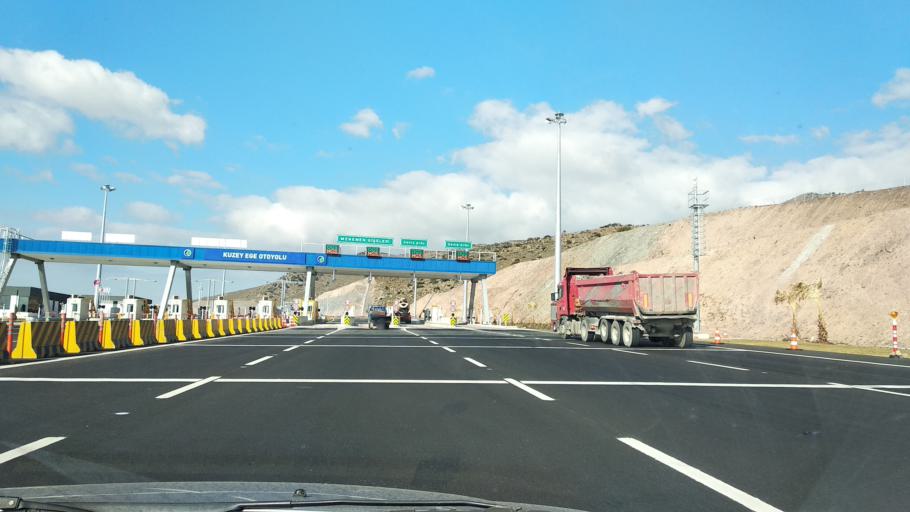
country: TR
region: Izmir
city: Menemen
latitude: 38.6729
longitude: 27.0637
